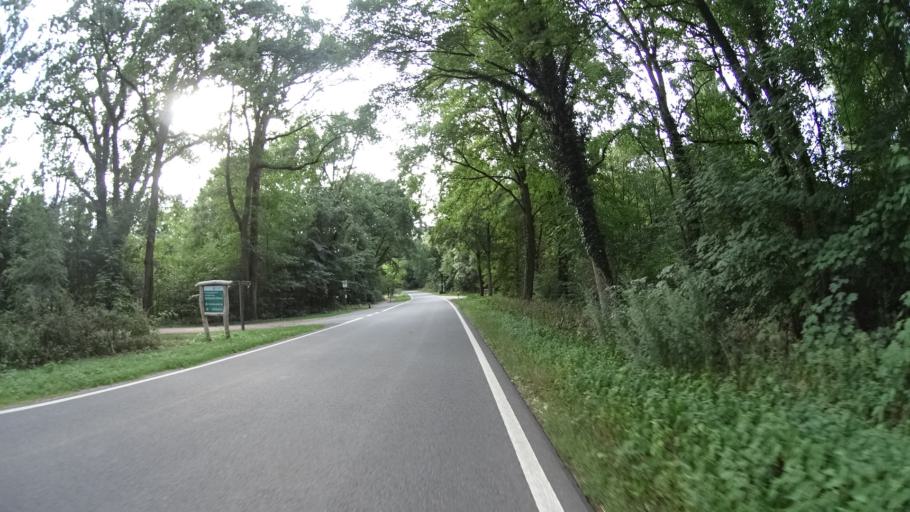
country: DE
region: Lower Saxony
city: Handeloh
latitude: 53.1773
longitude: 9.8845
